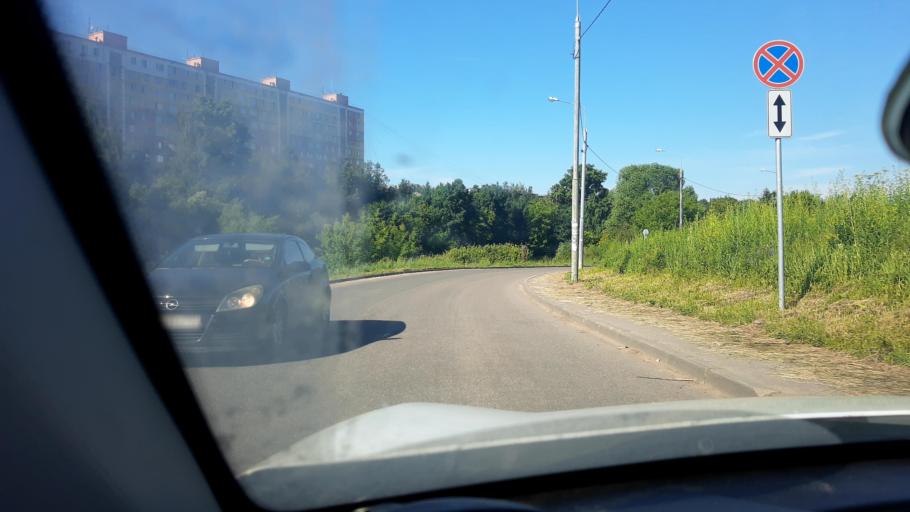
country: RU
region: Moskovskaya
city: Vidnoye
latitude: 55.5563
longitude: 37.6962
